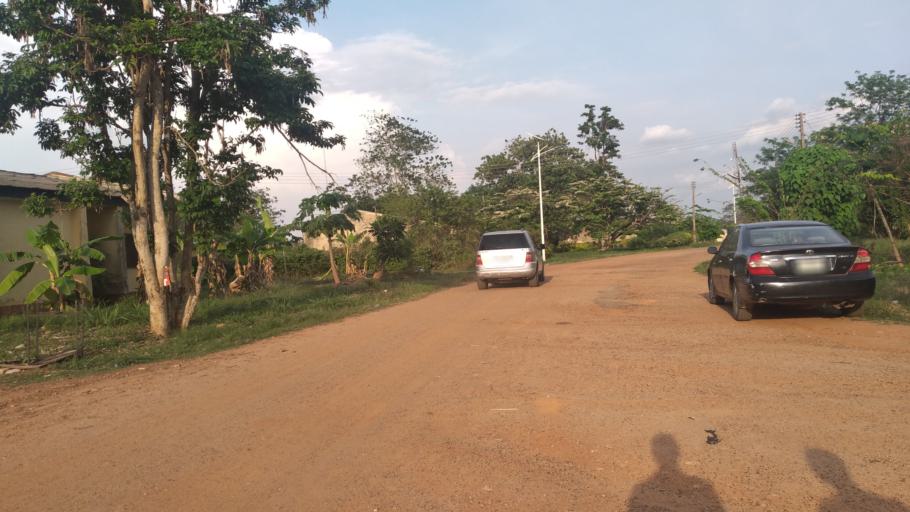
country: NG
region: Ondo
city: Ilare
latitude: 7.2972
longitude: 5.1465
